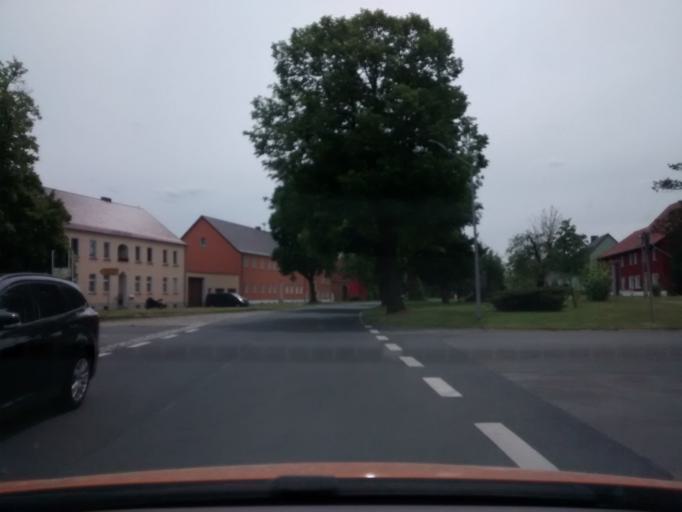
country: DE
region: Brandenburg
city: Juterbog
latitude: 51.9041
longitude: 13.1405
